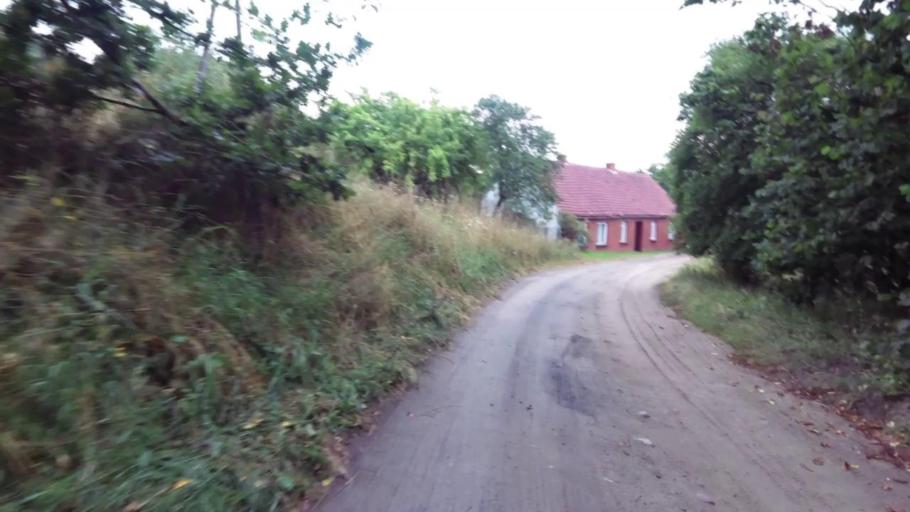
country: PL
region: West Pomeranian Voivodeship
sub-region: Powiat szczecinecki
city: Lubowo
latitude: 53.5882
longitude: 16.3871
